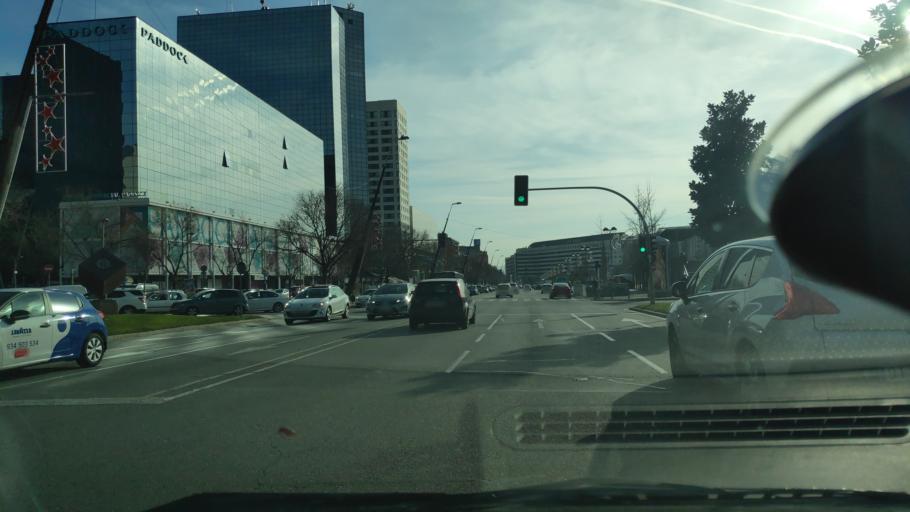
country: ES
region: Catalonia
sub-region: Provincia de Barcelona
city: Sabadell
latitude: 41.5541
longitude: 2.0976
